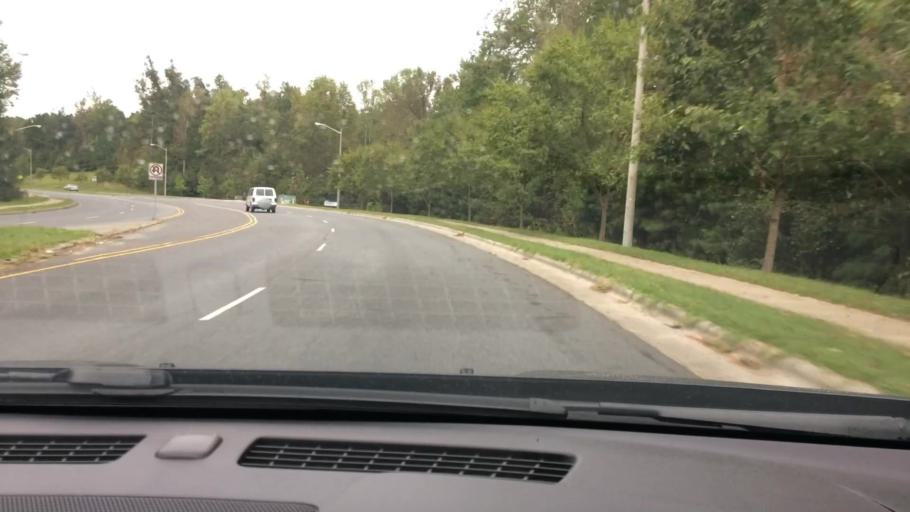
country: US
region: North Carolina
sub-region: Pitt County
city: Greenville
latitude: 35.6145
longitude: -77.4108
